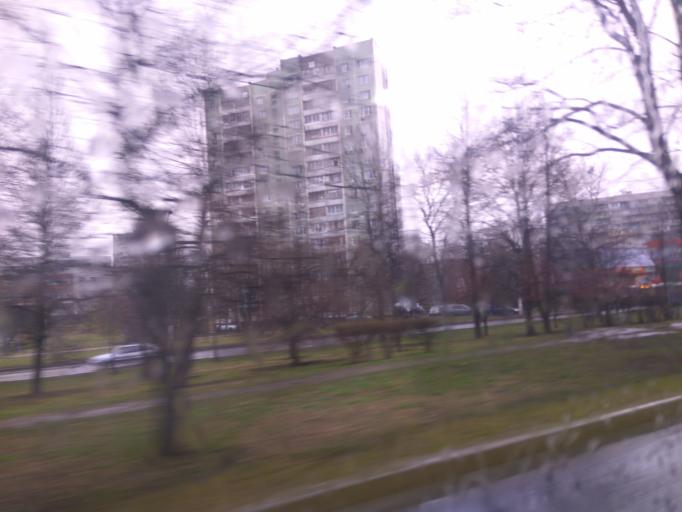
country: RU
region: Moscow
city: Bibirevo
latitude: 55.8943
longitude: 37.6142
